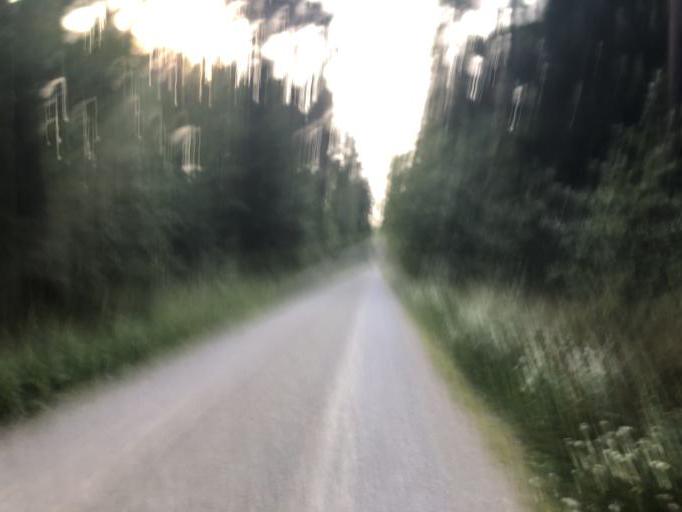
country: DE
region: Bavaria
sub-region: Regierungsbezirk Mittelfranken
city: Buckenhof
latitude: 49.5774
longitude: 11.0438
